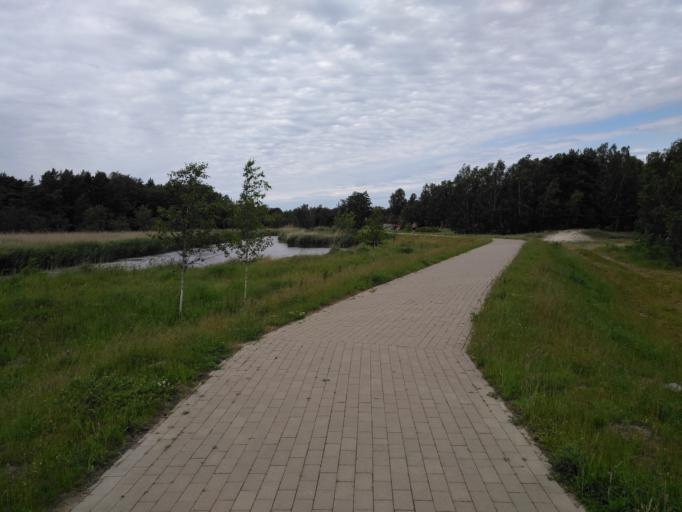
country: PL
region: West Pomeranian Voivodeship
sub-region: Powiat kolobrzeski
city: Grzybowo
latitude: 54.1526
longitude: 15.3906
